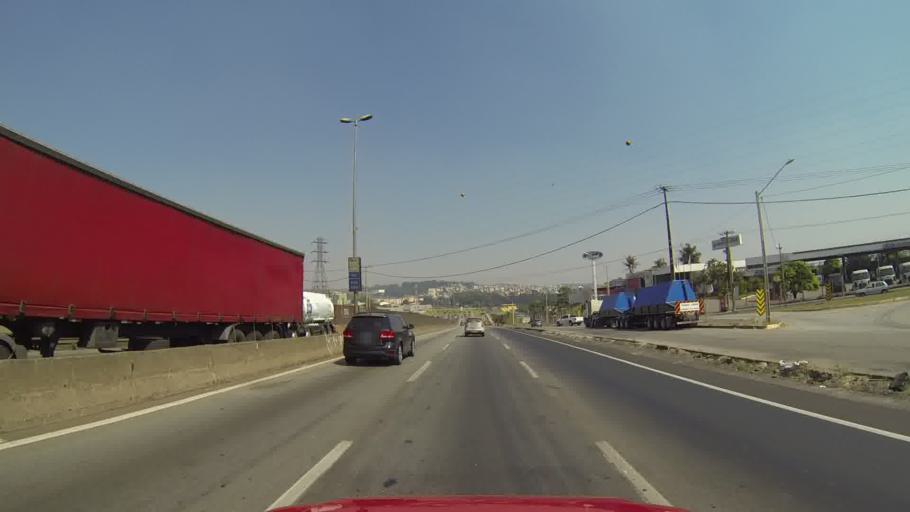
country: BR
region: Minas Gerais
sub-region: Contagem
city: Contagem
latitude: -19.9610
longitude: -44.0517
